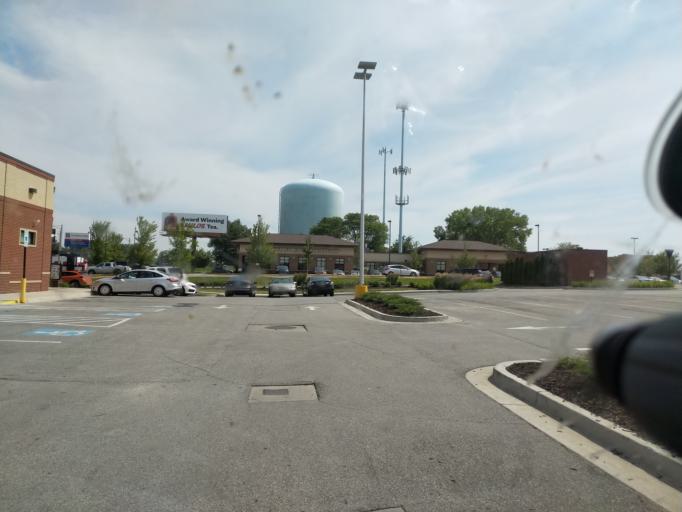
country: US
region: Iowa
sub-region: Polk County
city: Urbandale
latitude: 41.6353
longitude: -93.6984
